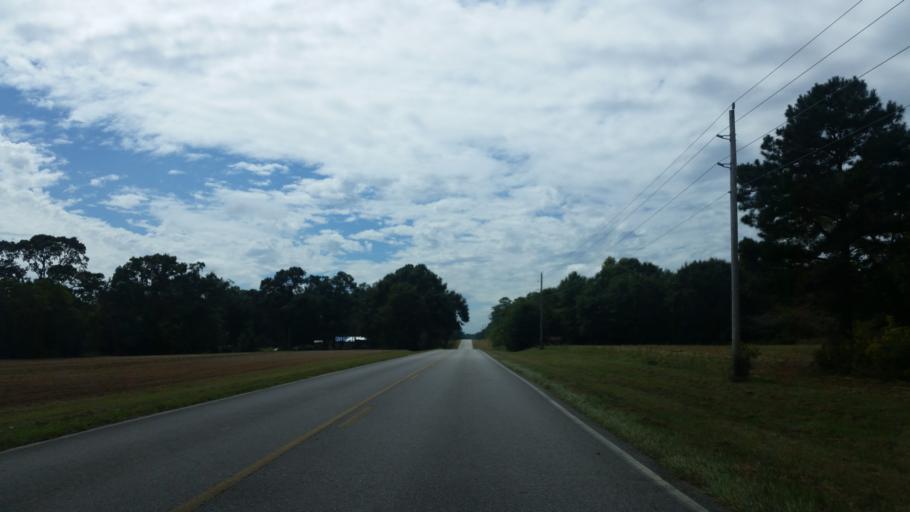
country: US
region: Florida
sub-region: Santa Rosa County
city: Point Baker
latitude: 30.8233
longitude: -86.9171
